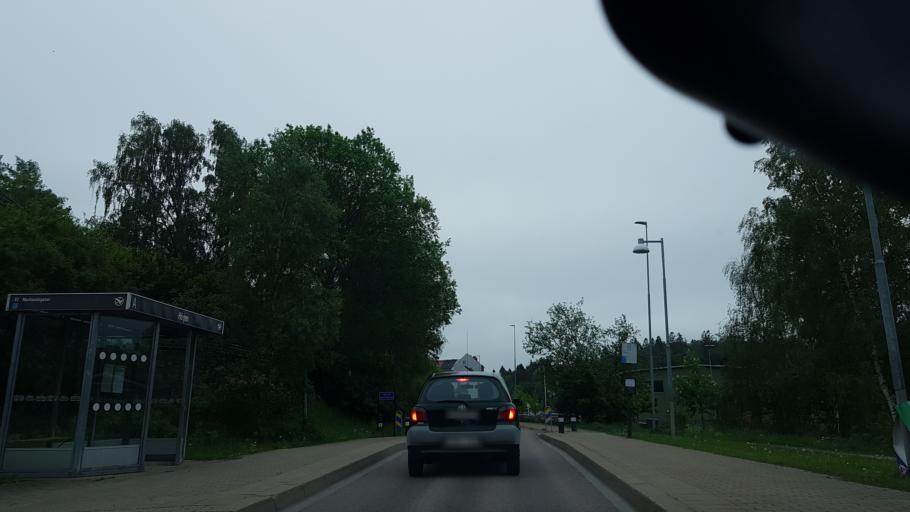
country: SE
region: Vaestra Goetaland
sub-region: Goteborg
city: Billdal
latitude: 57.6020
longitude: 11.9475
